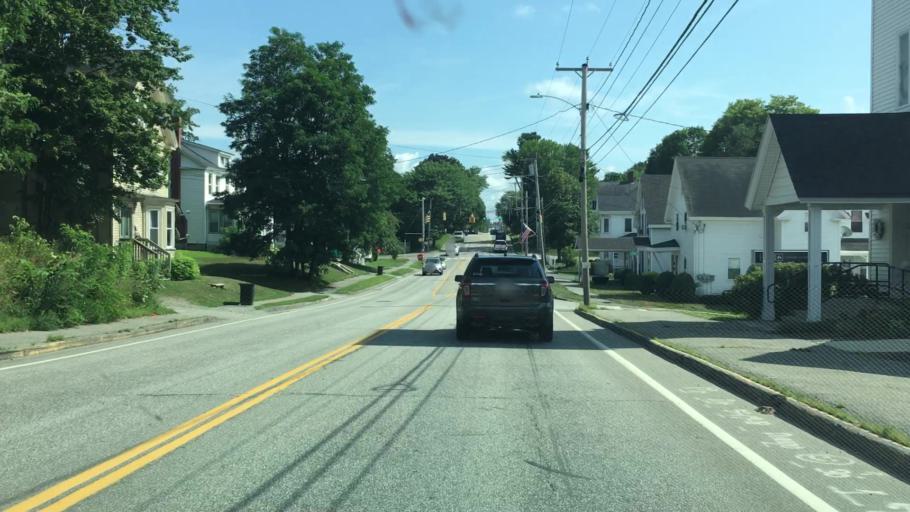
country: US
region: Maine
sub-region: Penobscot County
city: Brewer
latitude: 44.7956
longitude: -68.7603
